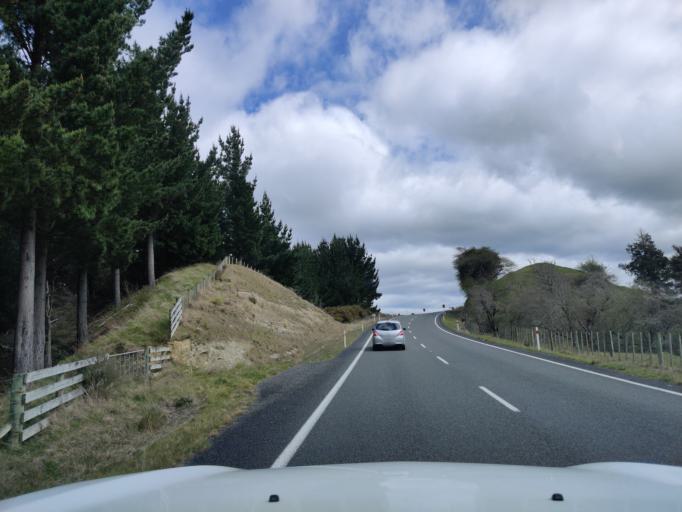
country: NZ
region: Manawatu-Wanganui
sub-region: Wanganui District
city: Wanganui
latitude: -39.7885
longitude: 175.2172
